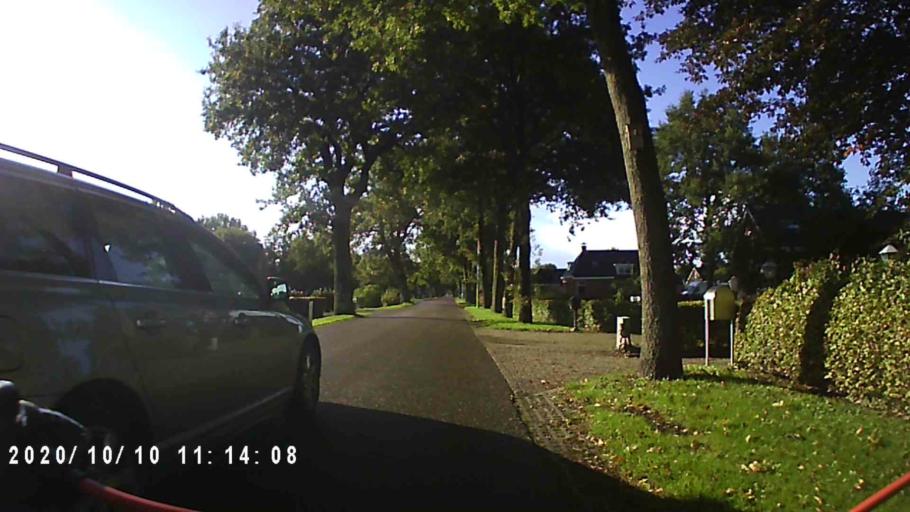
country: NL
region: Friesland
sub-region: Gemeente Smallingerland
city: Drachtstercompagnie
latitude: 53.1067
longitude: 6.2035
